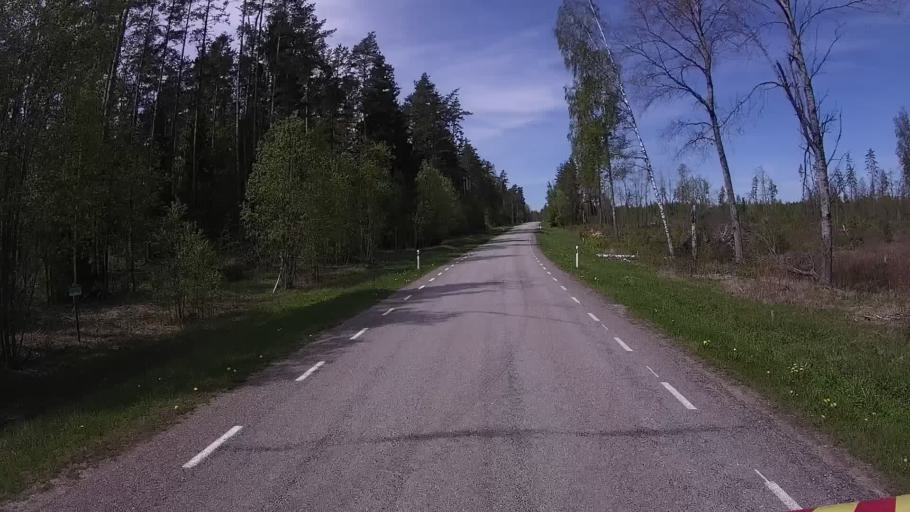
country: EE
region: Vorumaa
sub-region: Antsla vald
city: Vana-Antsla
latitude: 57.6171
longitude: 26.3570
